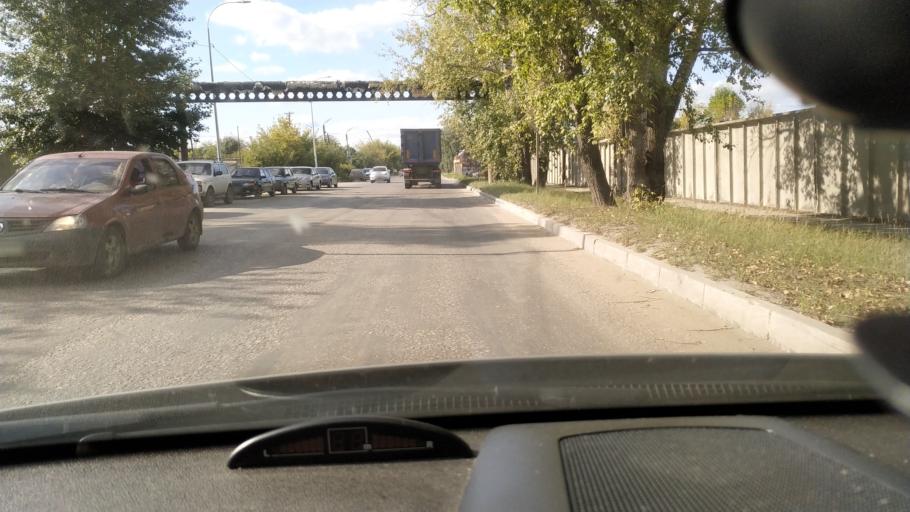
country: RU
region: Rjazan
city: Ryazan'
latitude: 54.6566
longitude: 39.6371
